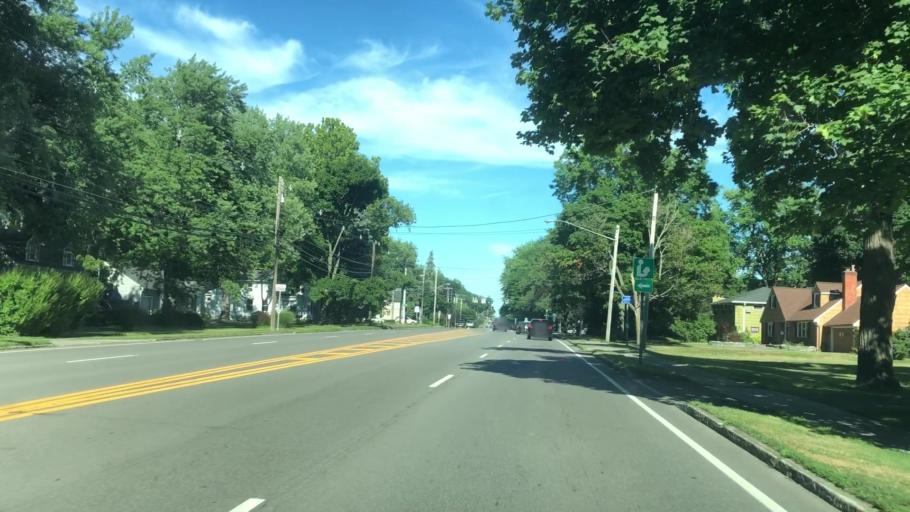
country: US
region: New York
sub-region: Monroe County
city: East Rochester
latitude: 43.1313
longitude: -77.4660
